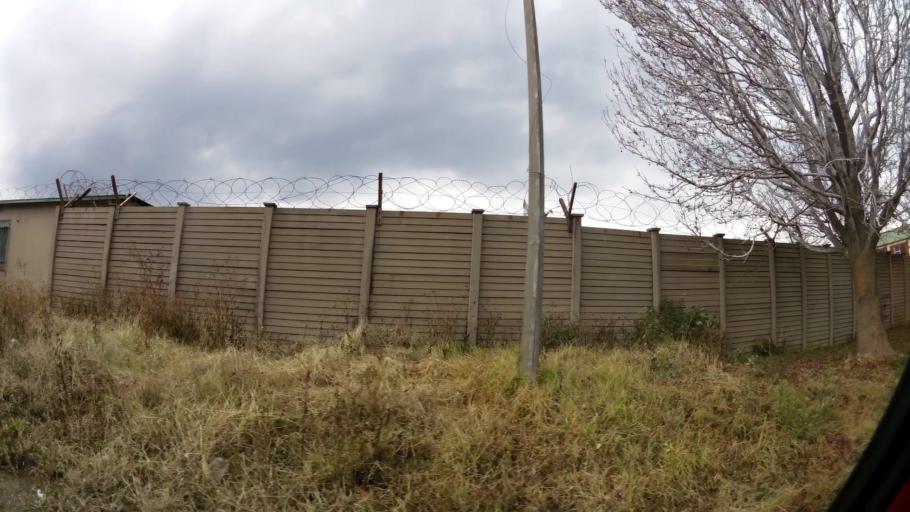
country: ZA
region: Gauteng
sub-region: Sedibeng District Municipality
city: Vanderbijlpark
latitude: -26.6889
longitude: 27.8075
